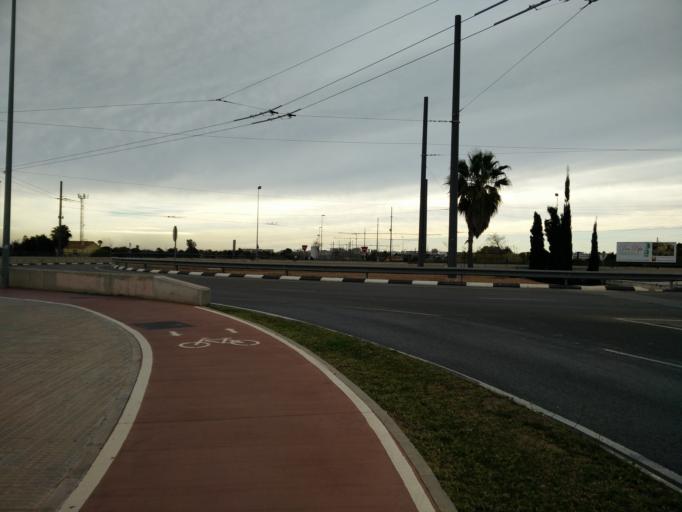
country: ES
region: Valencia
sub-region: Provincia de Castello
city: Castello de la Plana
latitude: 39.9811
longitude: -0.0106
